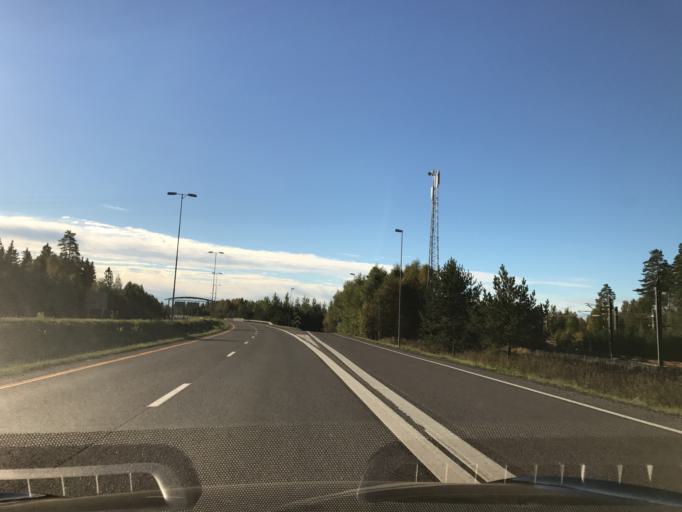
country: NO
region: Akershus
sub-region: Nannestad
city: Teigebyen
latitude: 60.1807
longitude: 11.0933
